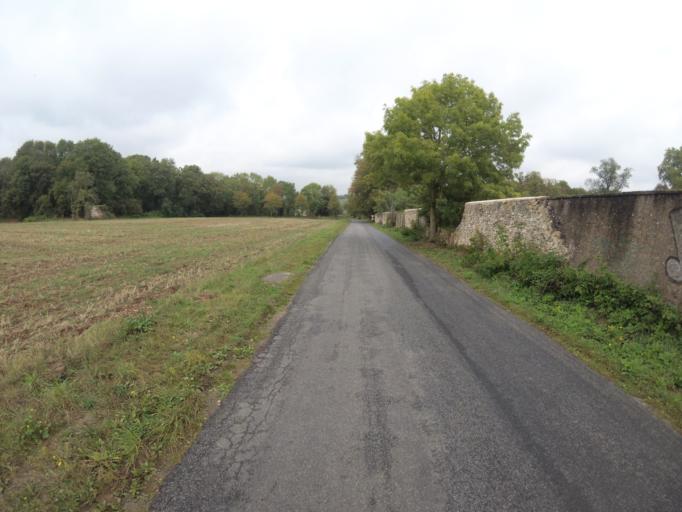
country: FR
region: Ile-de-France
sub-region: Departement de Seine-et-Marne
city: Gouvernes
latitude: 48.8528
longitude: 2.6914
